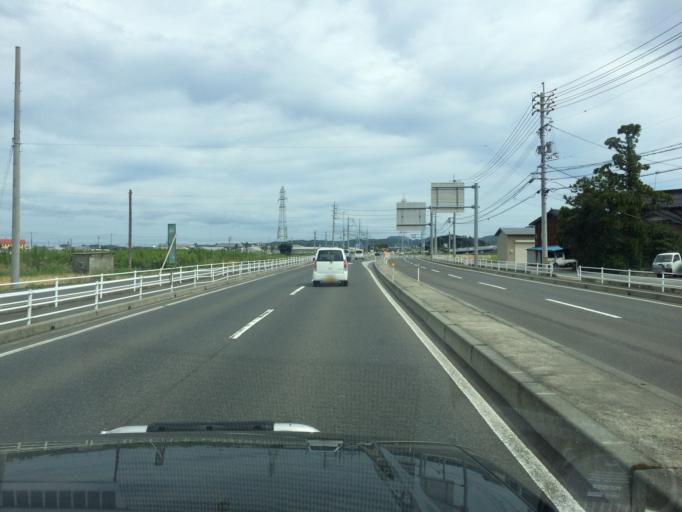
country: JP
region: Tottori
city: Tottori
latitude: 35.4943
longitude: 134.1917
